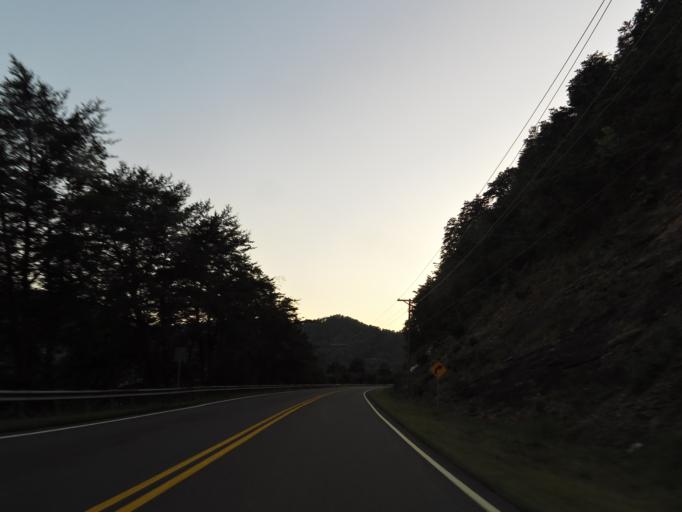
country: US
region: Tennessee
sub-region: Loudon County
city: Greenback
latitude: 35.5436
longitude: -84.0395
